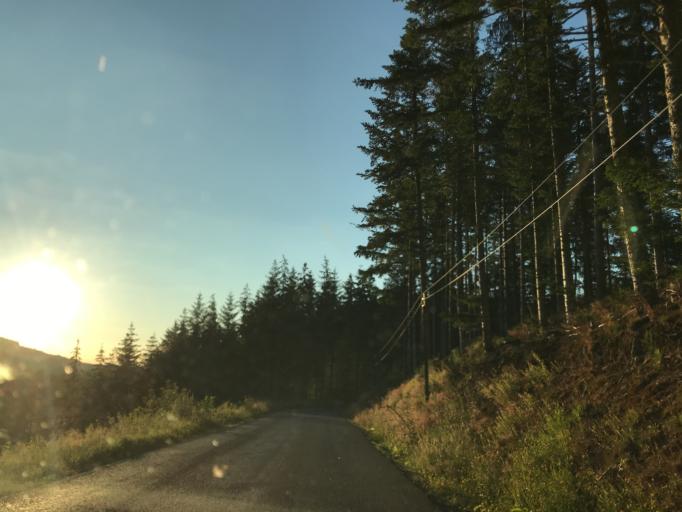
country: FR
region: Rhone-Alpes
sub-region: Departement de la Loire
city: Noiretable
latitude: 45.8101
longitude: 3.7319
